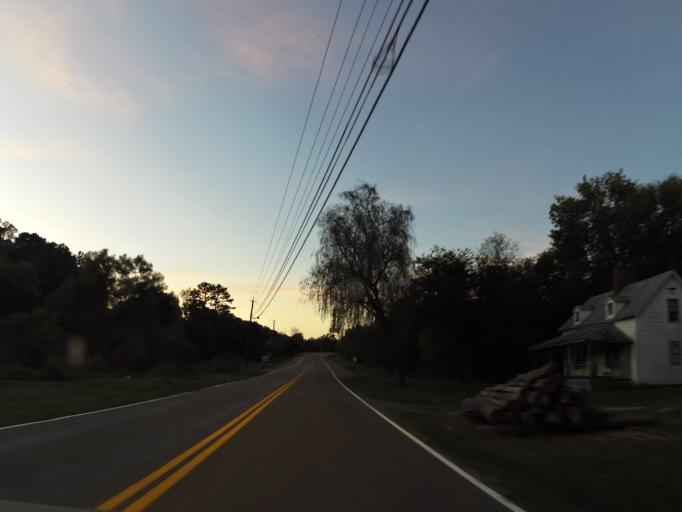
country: US
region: Tennessee
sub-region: Sevier County
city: Seymour
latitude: 35.9791
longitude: -83.6297
